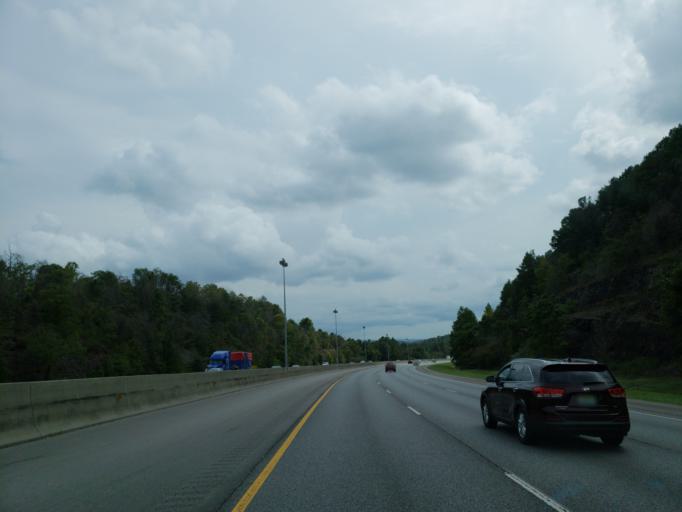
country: US
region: Alabama
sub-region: Jefferson County
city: Cahaba Heights
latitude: 33.4737
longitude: -86.7059
